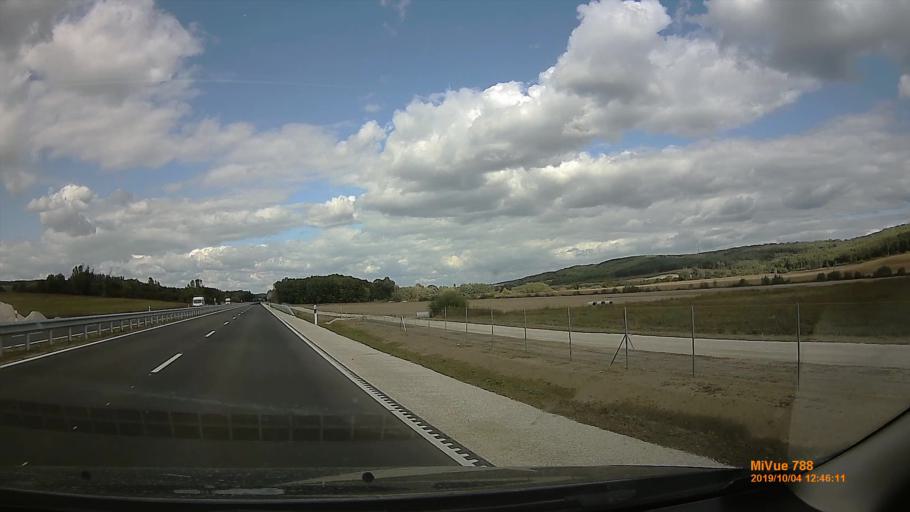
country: HU
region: Somogy
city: Karad
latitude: 46.6845
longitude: 17.7744
